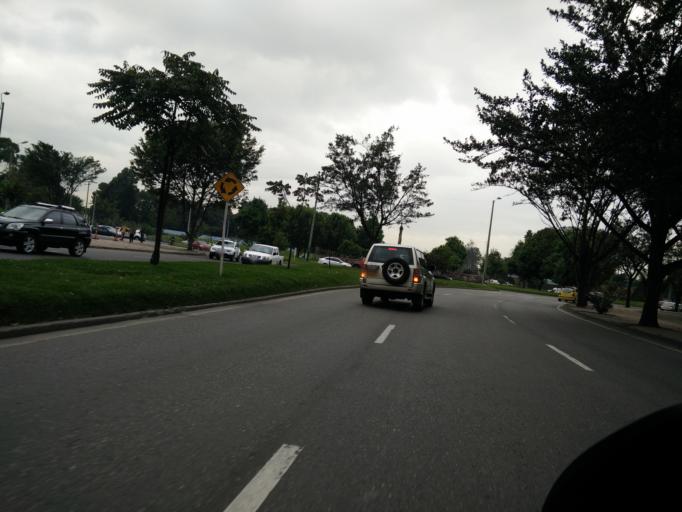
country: CO
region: Bogota D.C.
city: Bogota
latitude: 4.6585
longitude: -74.0879
